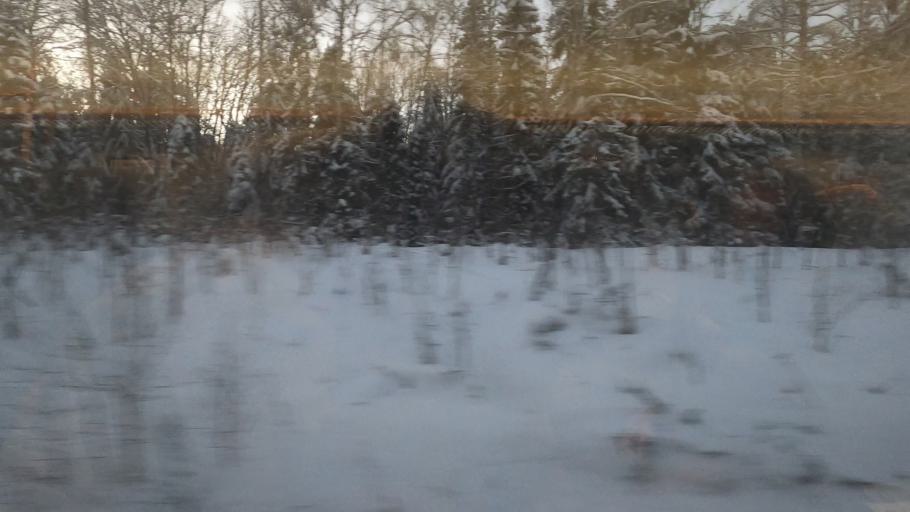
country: RU
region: Moskovskaya
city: Nekrasovskiy
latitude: 56.1150
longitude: 37.5111
